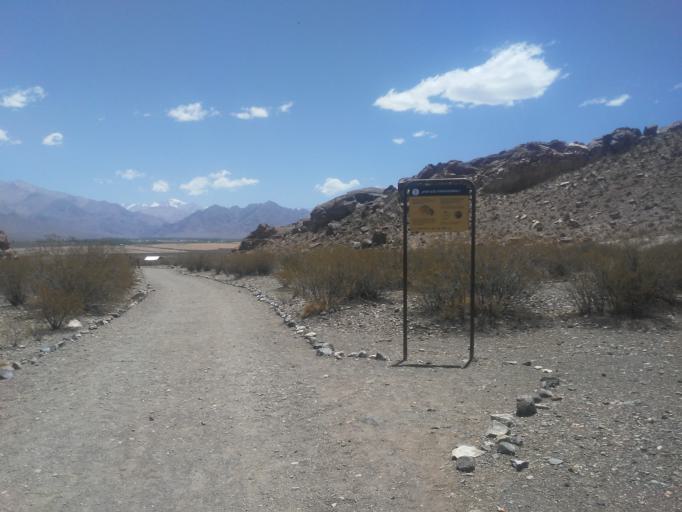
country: AR
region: Mendoza
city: Las Heras
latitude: -32.5312
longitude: -69.3090
